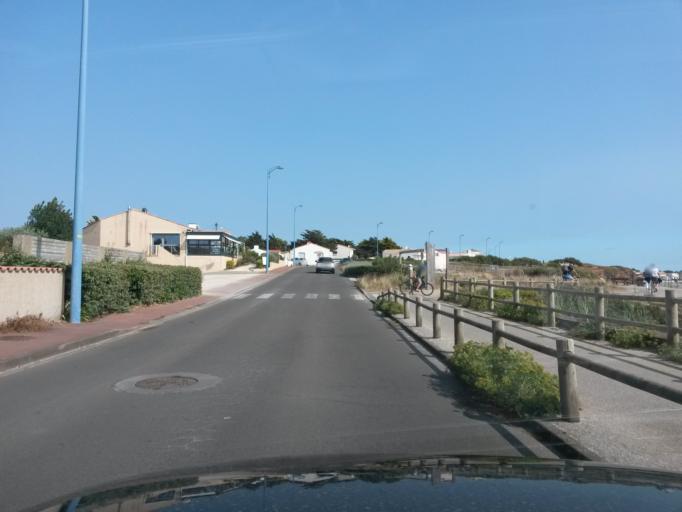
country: FR
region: Pays de la Loire
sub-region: Departement de la Vendee
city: Bretignolles-sur-Mer
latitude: 46.6317
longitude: -1.8825
